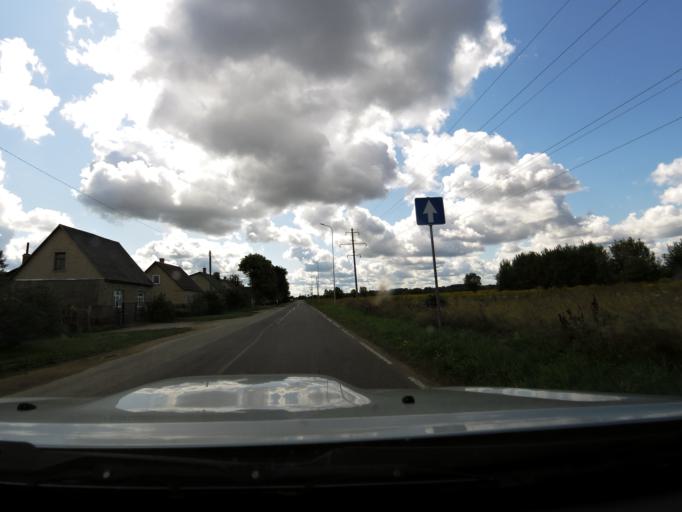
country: LV
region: Daugavpils
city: Daugavpils
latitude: 55.8692
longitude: 26.4921
